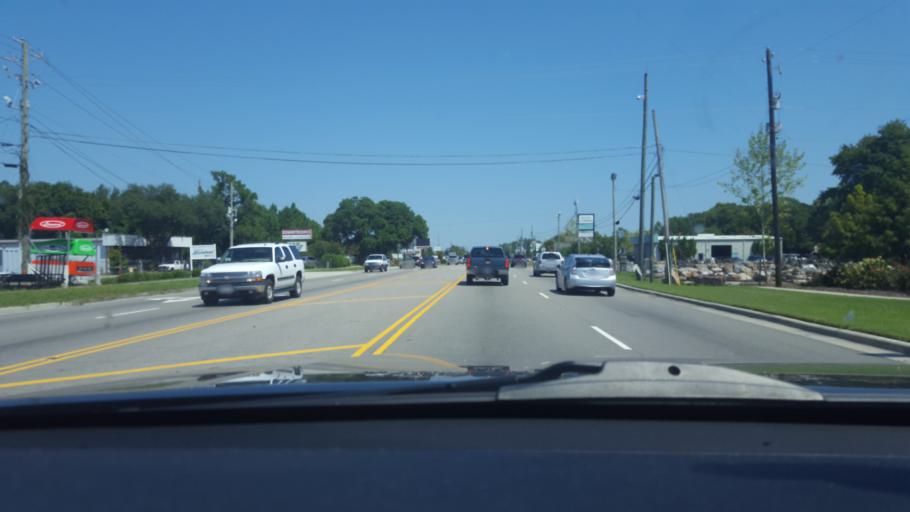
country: US
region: North Carolina
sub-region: New Hanover County
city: Kings Grant
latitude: 34.2487
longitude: -77.8618
